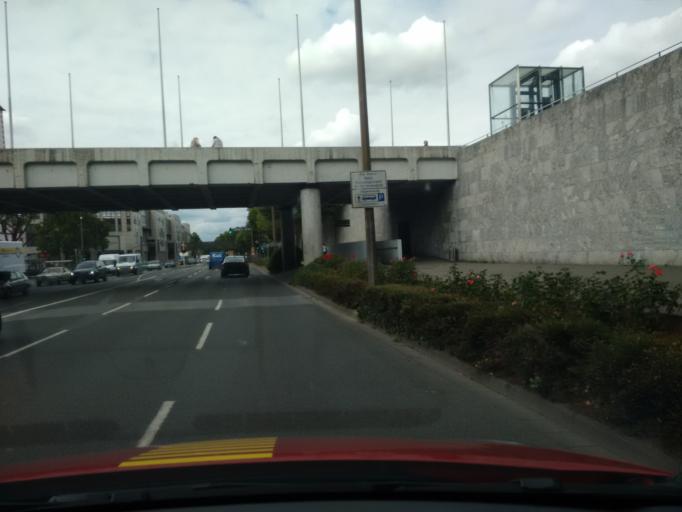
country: DE
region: Rheinland-Pfalz
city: Mainz
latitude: 50.0008
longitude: 8.2762
